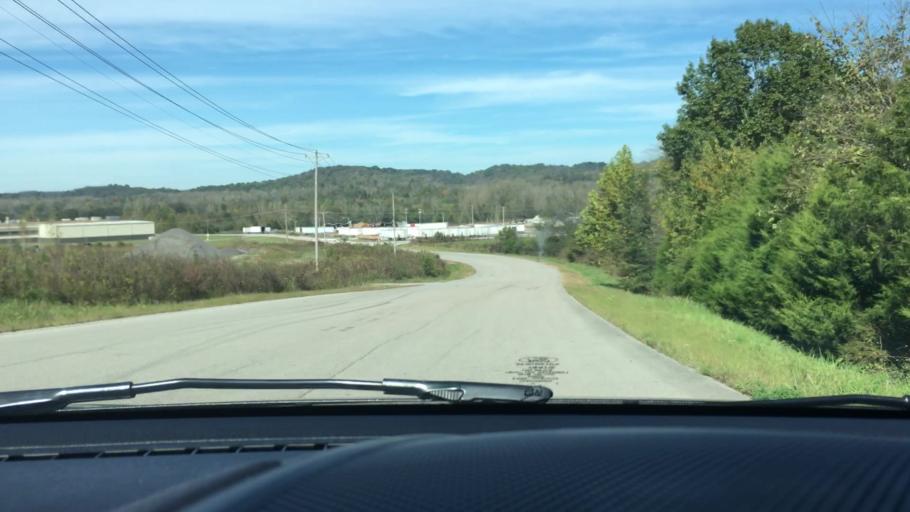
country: US
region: Tennessee
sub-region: Giles County
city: Pulaski
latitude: 35.2253
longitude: -87.0678
